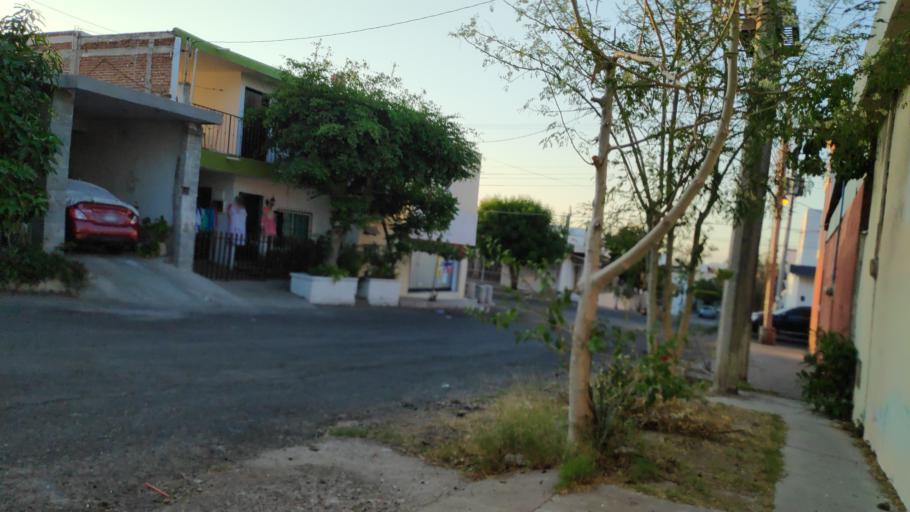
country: MX
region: Sinaloa
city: Culiacan
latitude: 24.7860
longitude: -107.4028
